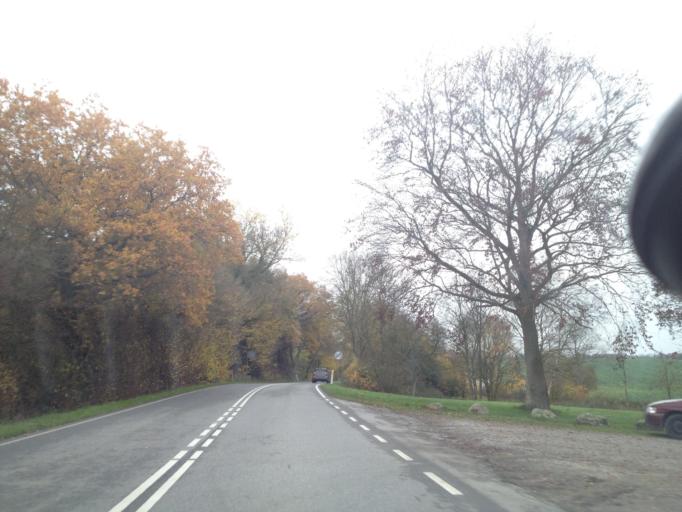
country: DK
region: South Denmark
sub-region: Assens Kommune
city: Vissenbjerg
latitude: 55.4493
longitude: 10.1341
